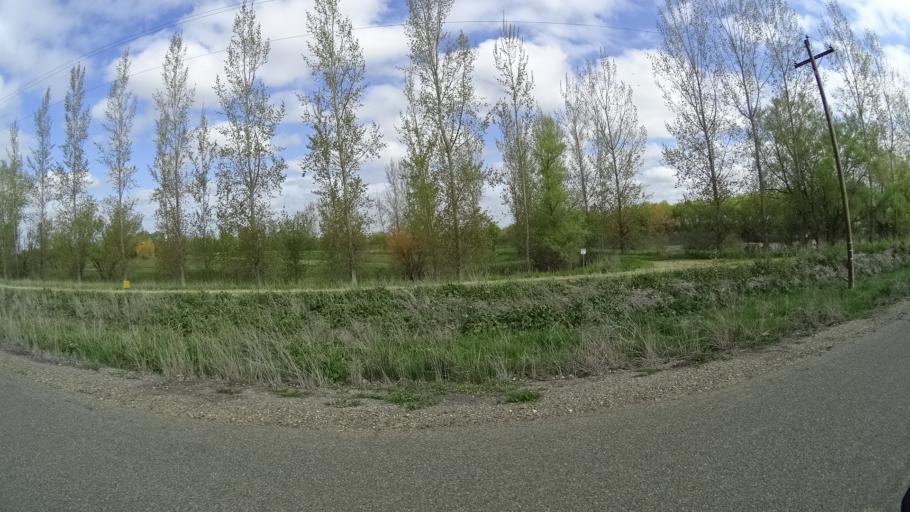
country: US
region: California
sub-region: Butte County
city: Biggs
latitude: 39.4203
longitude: -121.9170
